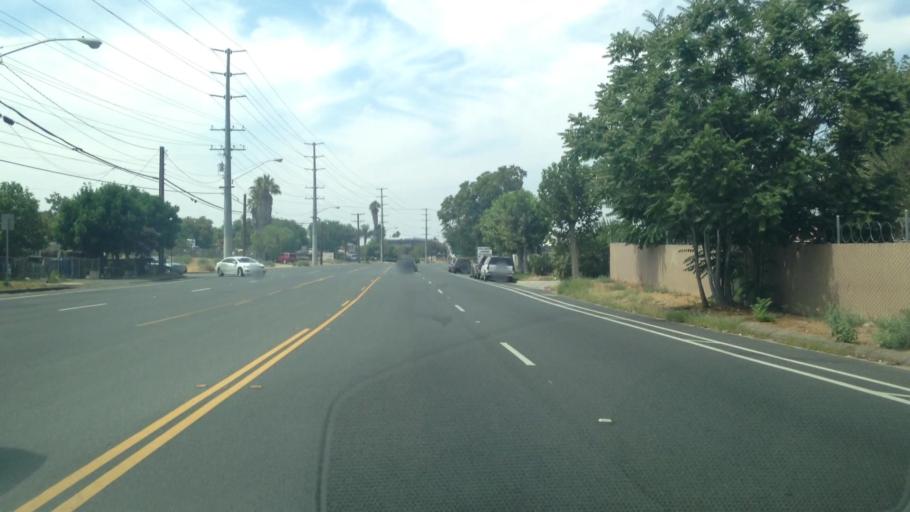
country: US
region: California
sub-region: Riverside County
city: Pedley
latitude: 33.9624
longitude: -117.4366
